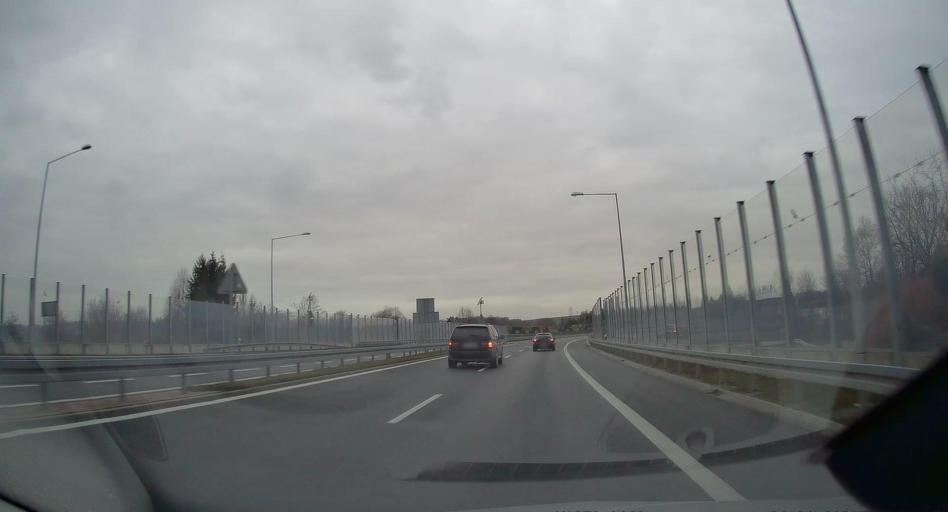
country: PL
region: Subcarpathian Voivodeship
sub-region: Powiat ropczycko-sedziszowski
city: Ropczyce
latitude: 50.0502
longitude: 21.6022
